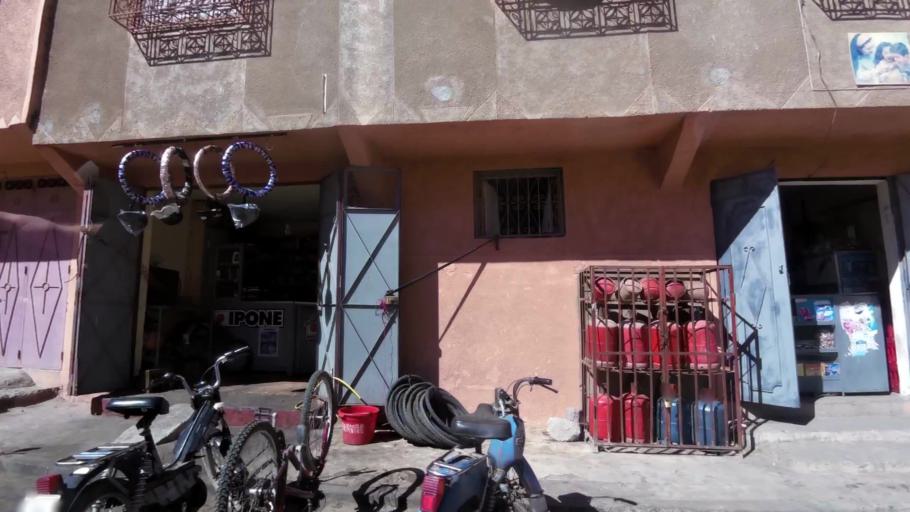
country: MA
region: Marrakech-Tensift-Al Haouz
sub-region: Marrakech
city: Marrakesh
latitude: 31.5914
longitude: -8.0487
